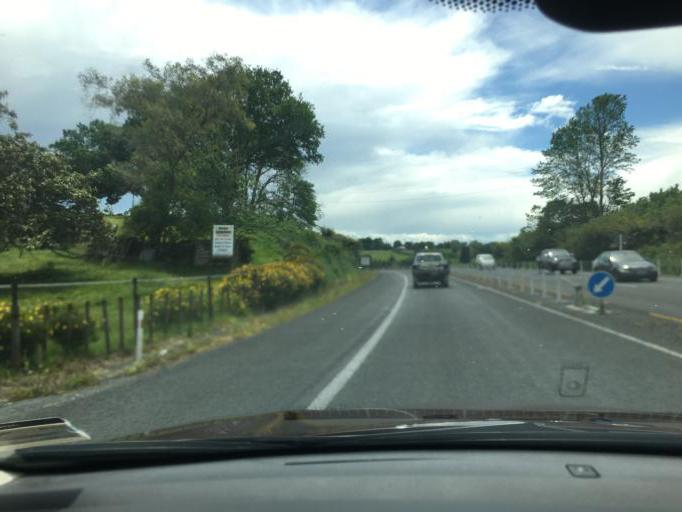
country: NZ
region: Waikato
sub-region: Waipa District
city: Cambridge
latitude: -37.9557
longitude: 175.3183
